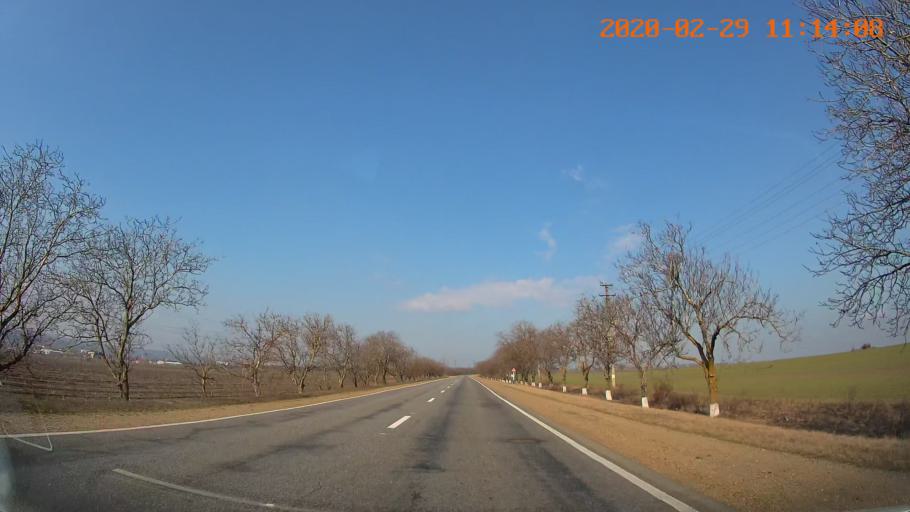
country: MD
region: Telenesti
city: Dubasari
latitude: 47.2791
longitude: 29.1756
